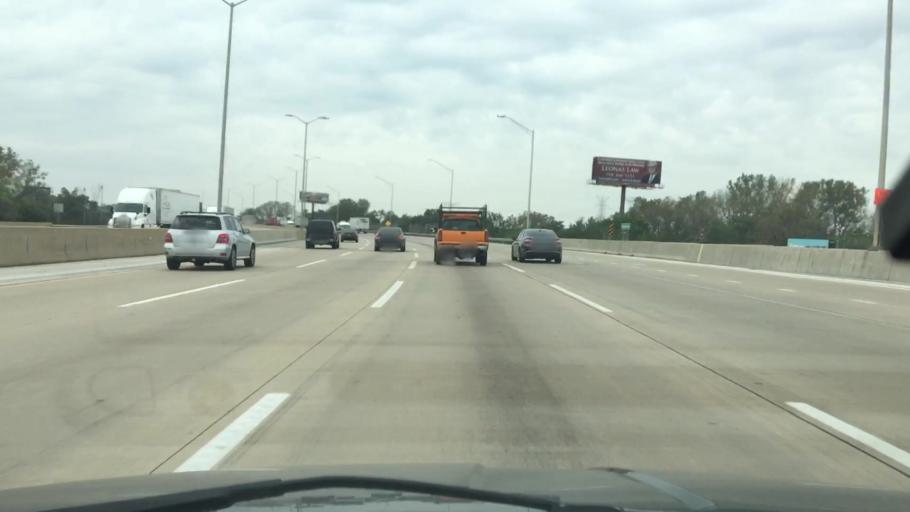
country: US
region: Illinois
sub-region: Cook County
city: Robbins
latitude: 41.6323
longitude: -87.6977
